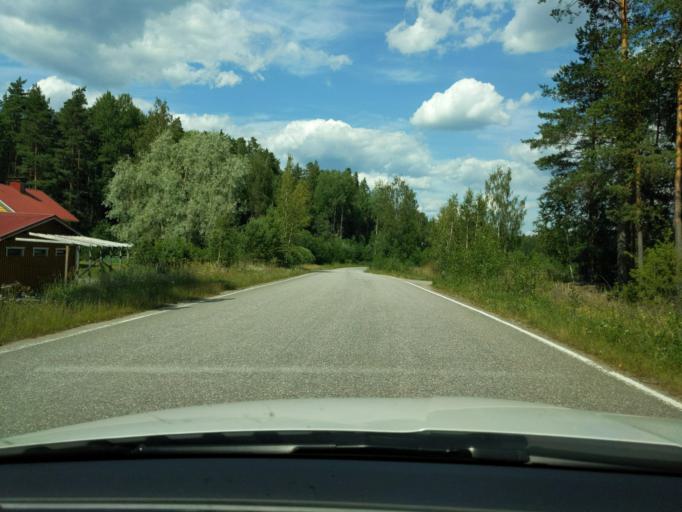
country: FI
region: Paijanne Tavastia
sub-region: Lahti
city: Heinola
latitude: 61.3367
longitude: 26.1724
